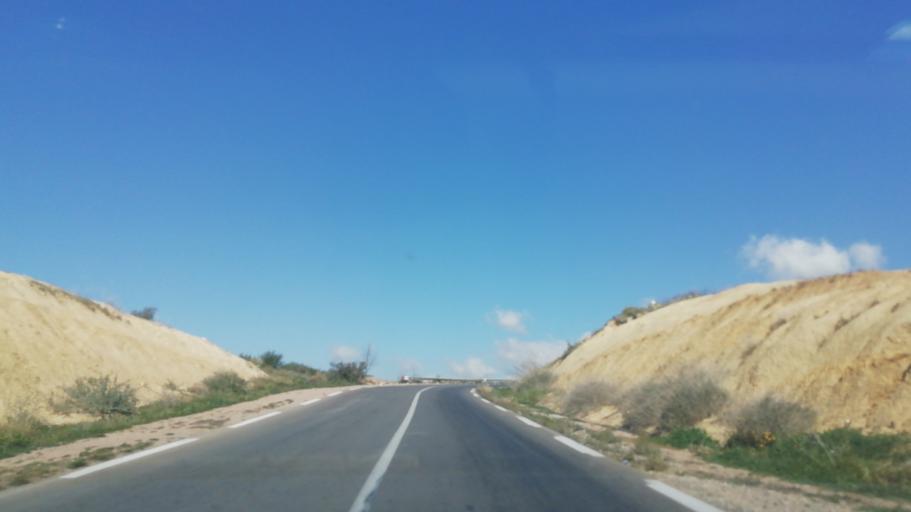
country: DZ
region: Mascara
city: Mascara
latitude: 35.4924
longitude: 0.1340
